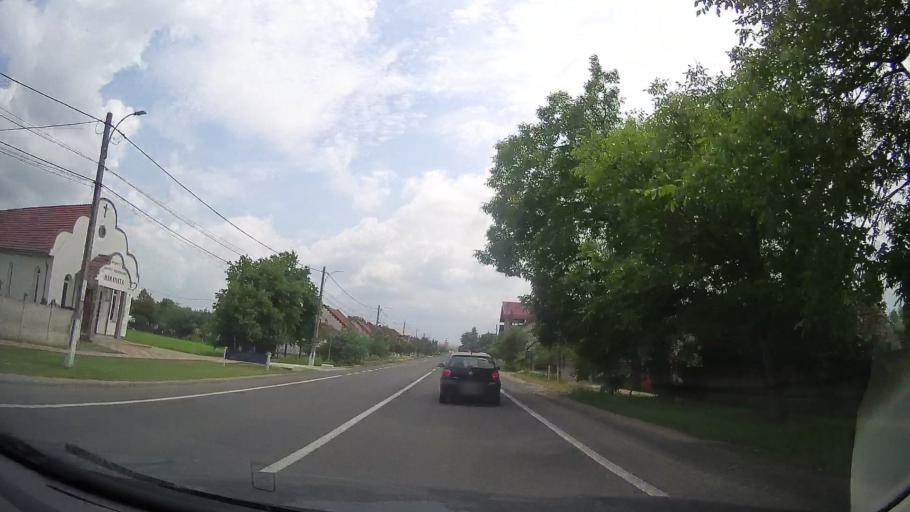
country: RO
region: Timis
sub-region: Comuna Costeiu
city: Costeiu
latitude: 45.7351
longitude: 21.8580
